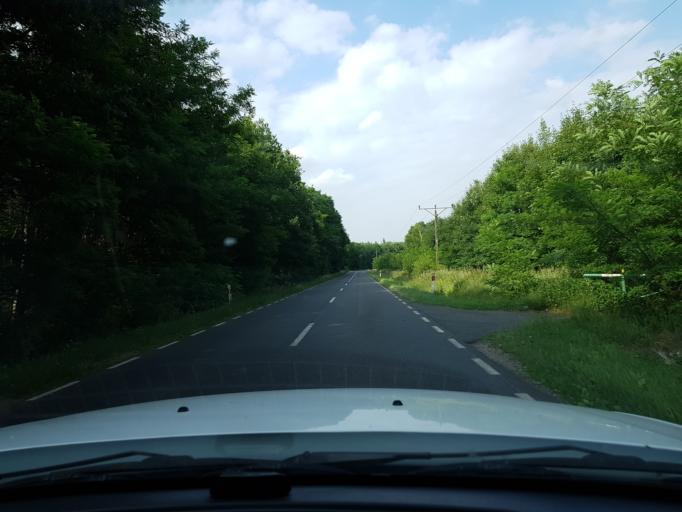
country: PL
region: West Pomeranian Voivodeship
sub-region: Powiat gryfinski
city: Chojna
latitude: 52.9302
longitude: 14.3756
